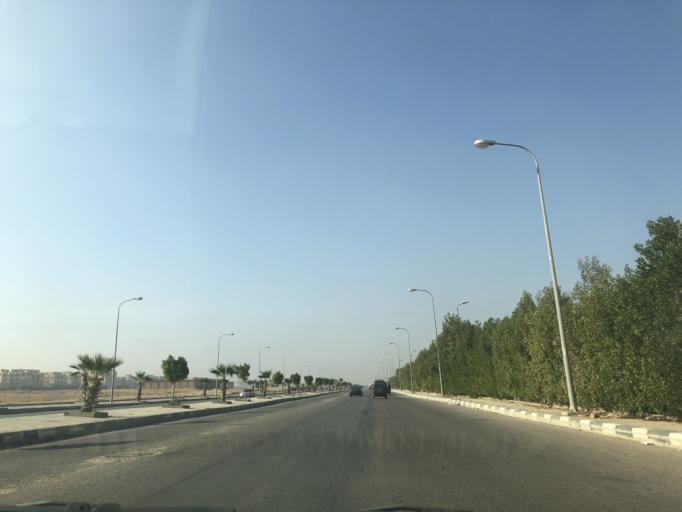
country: EG
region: Al Jizah
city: Madinat Sittah Uktubar
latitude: 29.9262
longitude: 31.0523
